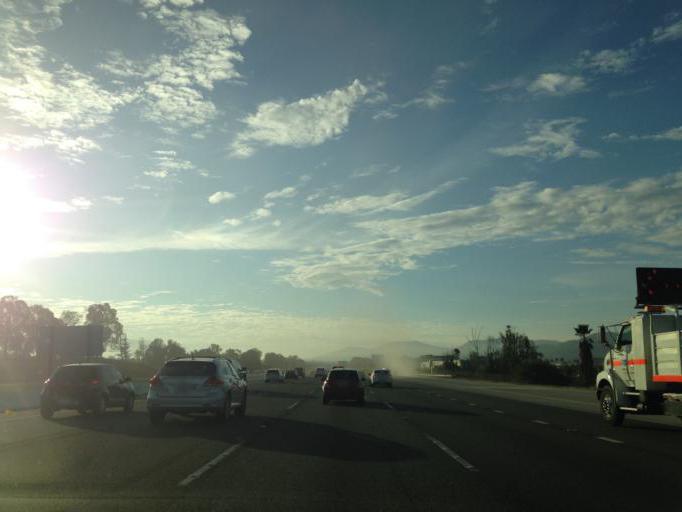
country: US
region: California
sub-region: Riverside County
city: Murrieta Hot Springs
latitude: 33.5302
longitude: -117.1684
